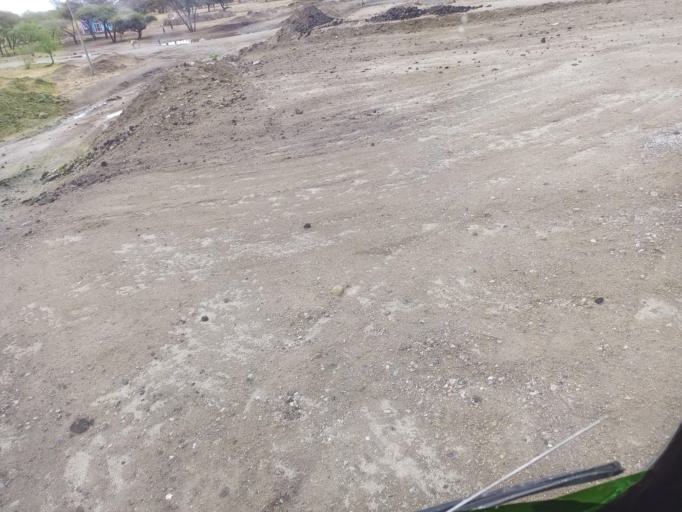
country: ET
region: Oromiya
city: Ziway
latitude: 7.5863
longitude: 38.6764
